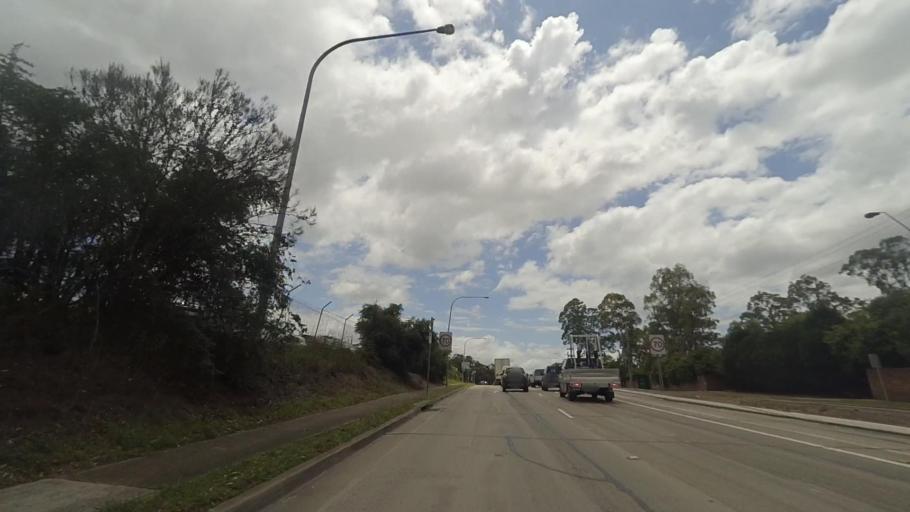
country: AU
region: New South Wales
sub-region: Fairfield
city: Cabramatta West
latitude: -33.9008
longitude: 150.9187
